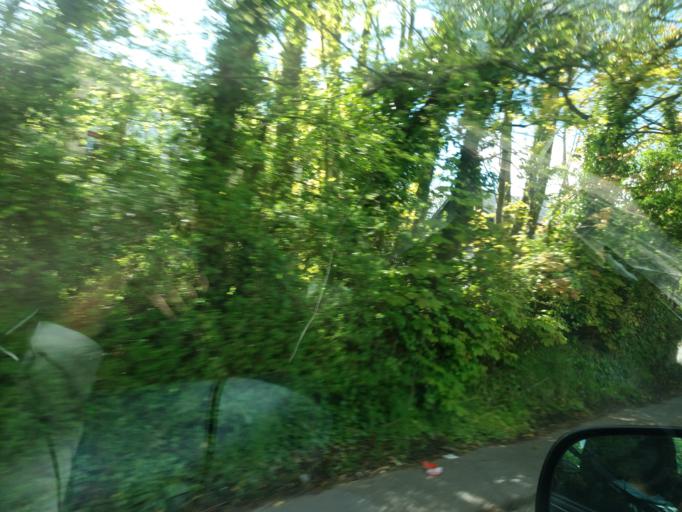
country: IE
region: Munster
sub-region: Waterford
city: Waterford
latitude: 52.2380
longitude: -7.0630
